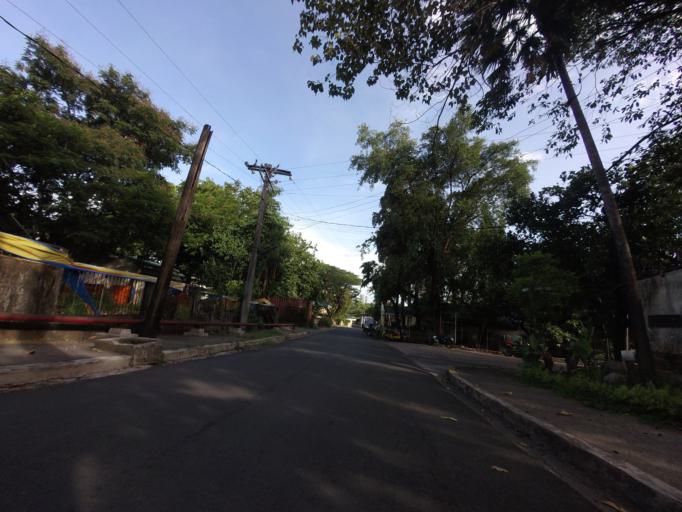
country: PH
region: Metro Manila
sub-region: Mandaluyong
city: Mandaluyong City
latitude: 14.5814
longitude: 121.0411
